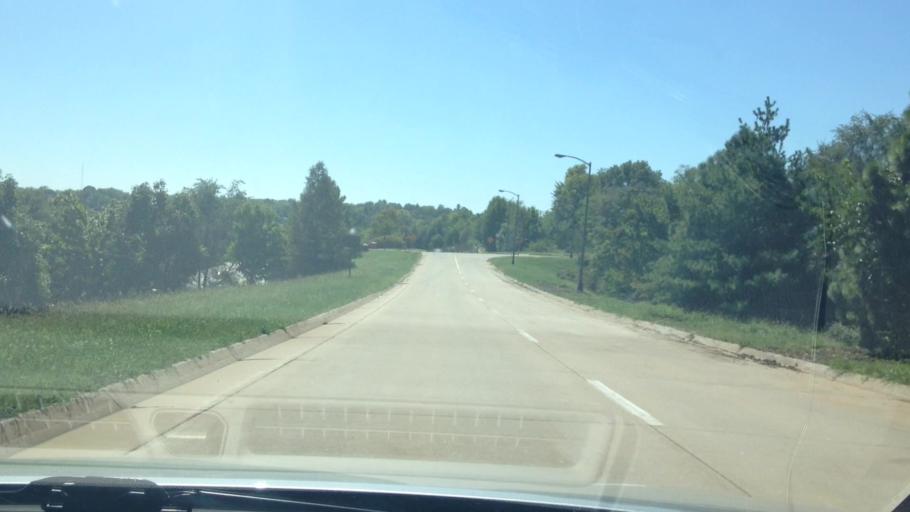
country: US
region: Missouri
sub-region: Jackson County
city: Kansas City
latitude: 39.0499
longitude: -94.5624
